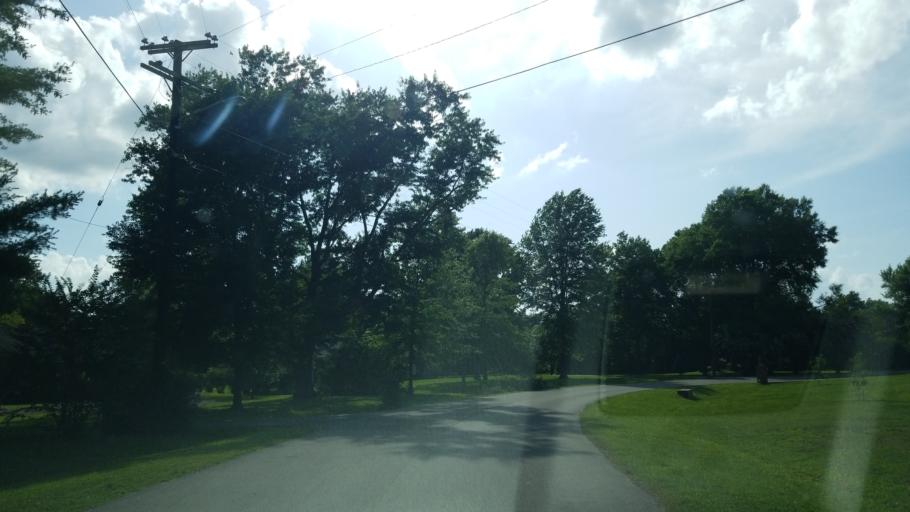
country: US
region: Tennessee
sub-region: Davidson County
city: Forest Hills
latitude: 36.0422
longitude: -86.8547
